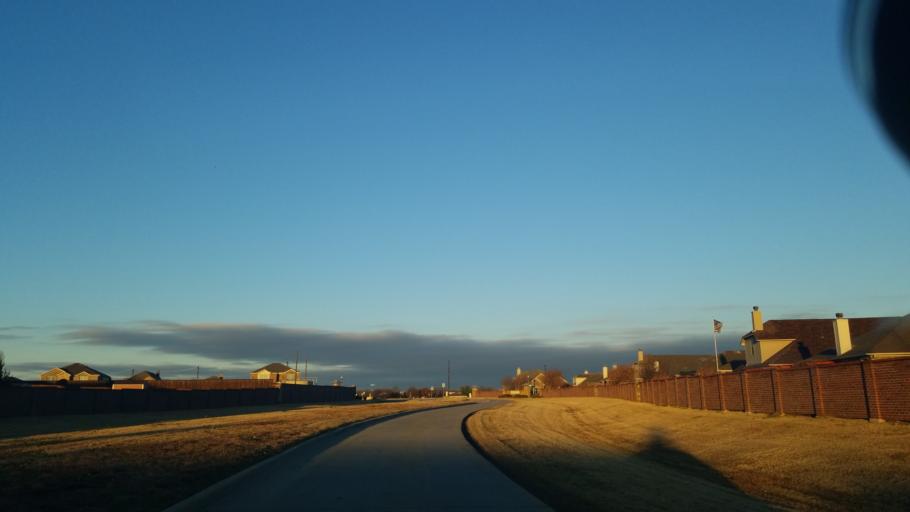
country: US
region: Texas
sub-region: Denton County
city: Argyle
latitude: 33.1699
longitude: -97.1646
